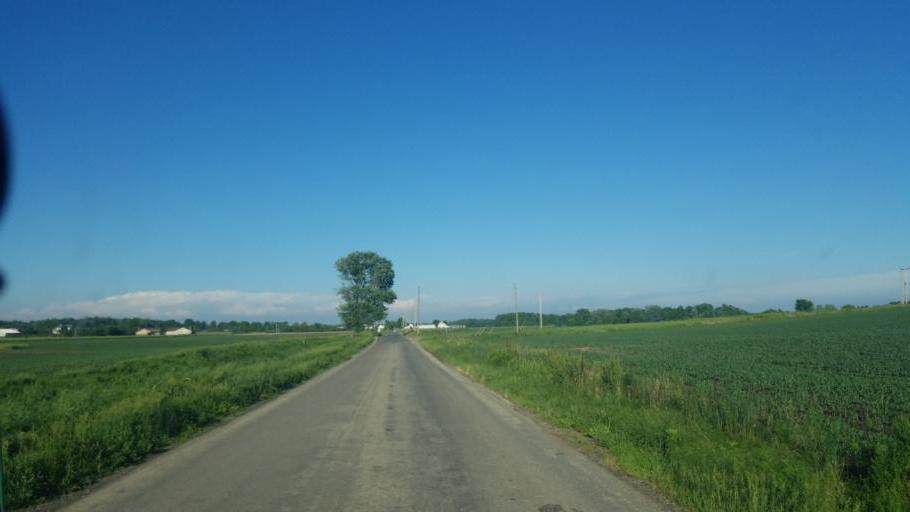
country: US
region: Indiana
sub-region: Marshall County
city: Bremen
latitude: 41.4265
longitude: -86.0847
